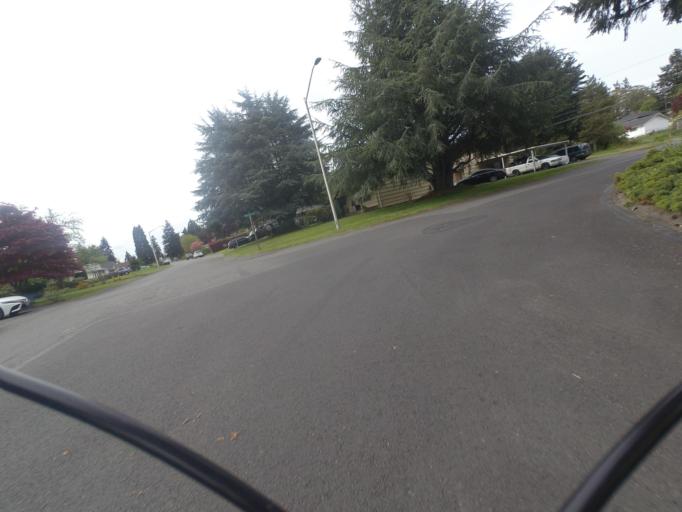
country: US
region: Washington
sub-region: Pierce County
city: McChord Air Force Base
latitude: 47.1617
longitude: -122.4875
